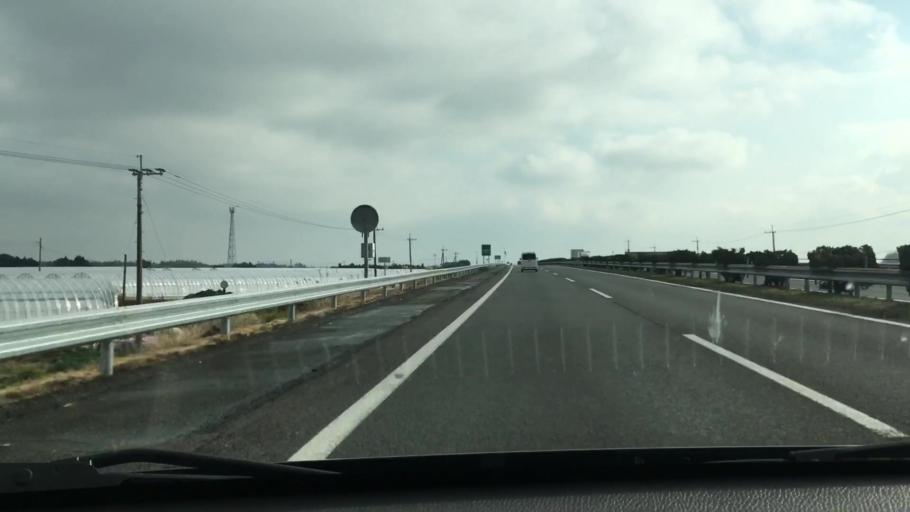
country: JP
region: Kumamoto
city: Ueki
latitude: 32.8910
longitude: 130.7212
